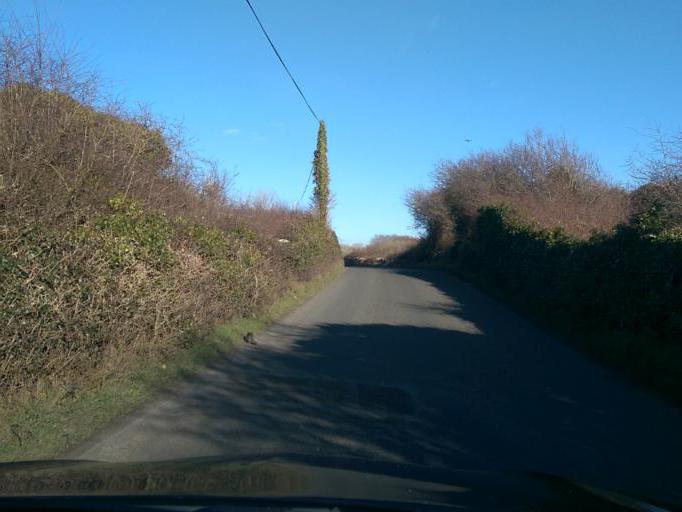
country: IE
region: Connaught
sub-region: County Galway
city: Oranmore
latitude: 53.2250
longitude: -8.9028
